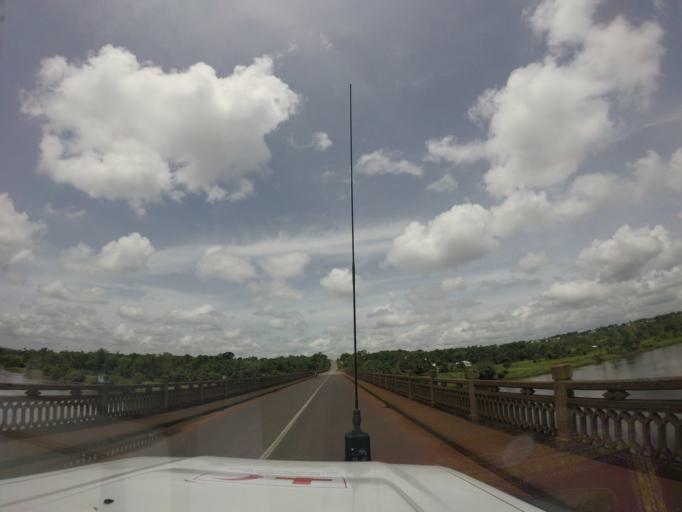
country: SL
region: Northern Province
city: Kambia
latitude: 9.1195
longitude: -12.9319
